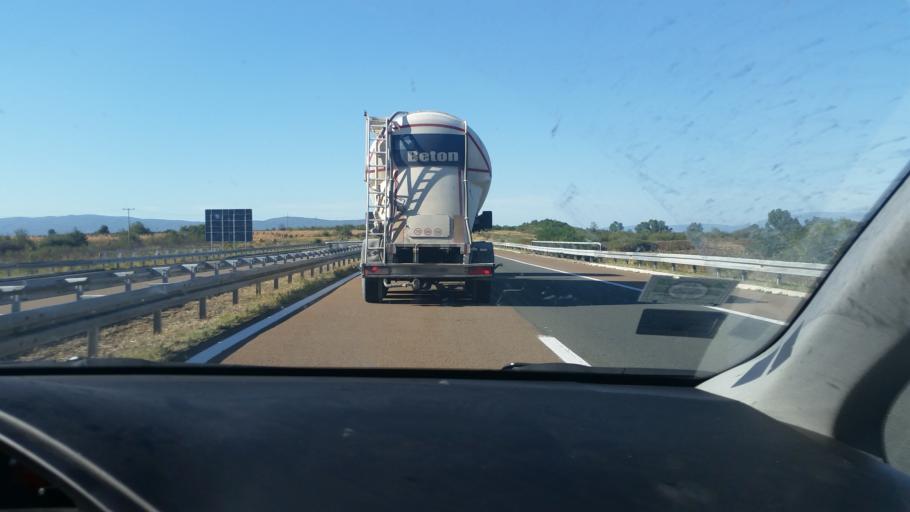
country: RS
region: Central Serbia
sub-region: Nisavski Okrug
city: Doljevac
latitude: 43.2720
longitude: 21.8065
